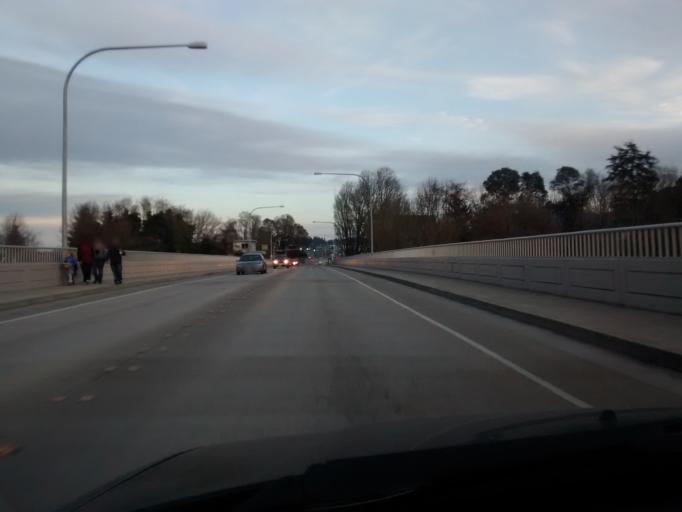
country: US
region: Washington
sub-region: Clallam County
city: Port Angeles
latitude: 48.1157
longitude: -123.4458
